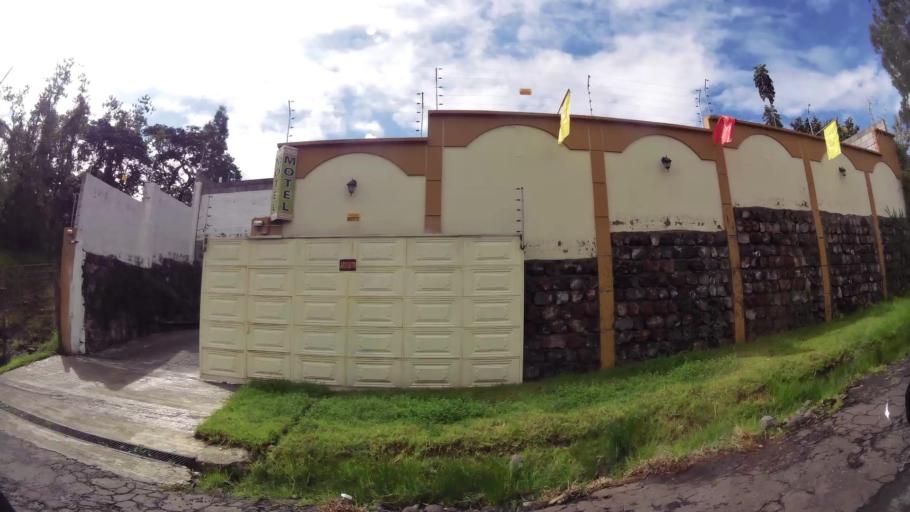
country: EC
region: Pichincha
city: Sangolqui
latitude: -0.3055
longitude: -78.4231
